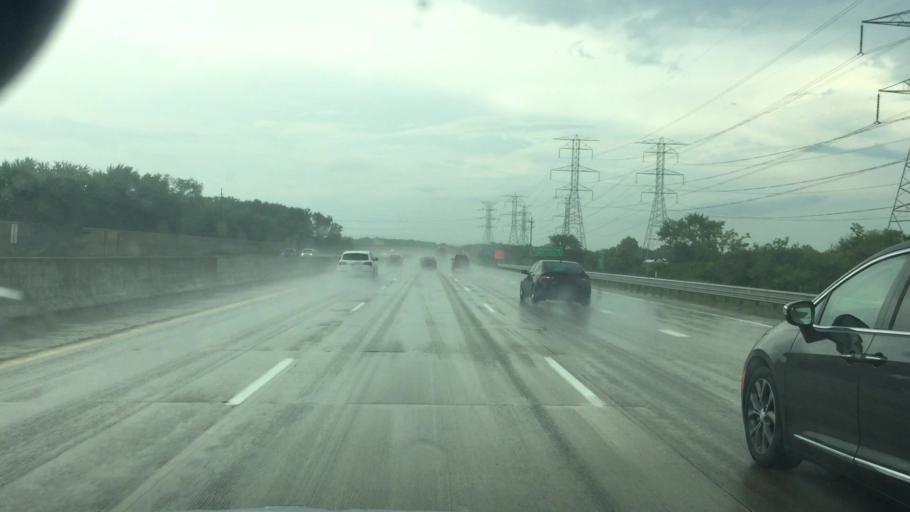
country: US
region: Michigan
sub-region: Wayne County
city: Rockwood
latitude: 42.0752
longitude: -83.2483
